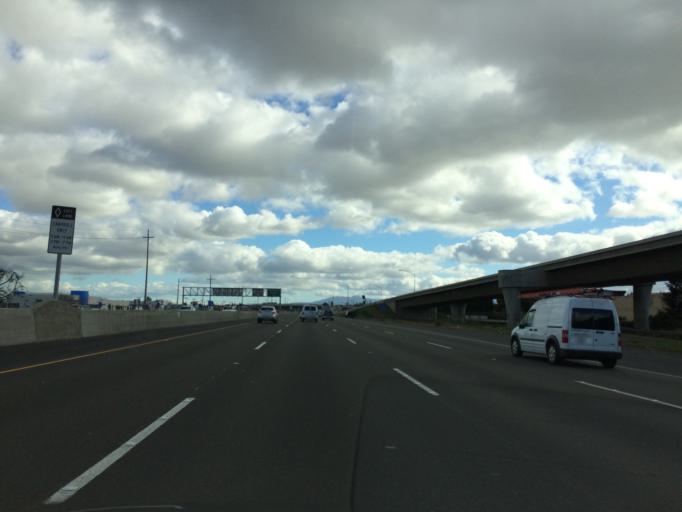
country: US
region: California
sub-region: Santa Clara County
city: Milpitas
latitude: 37.4220
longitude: -121.9155
